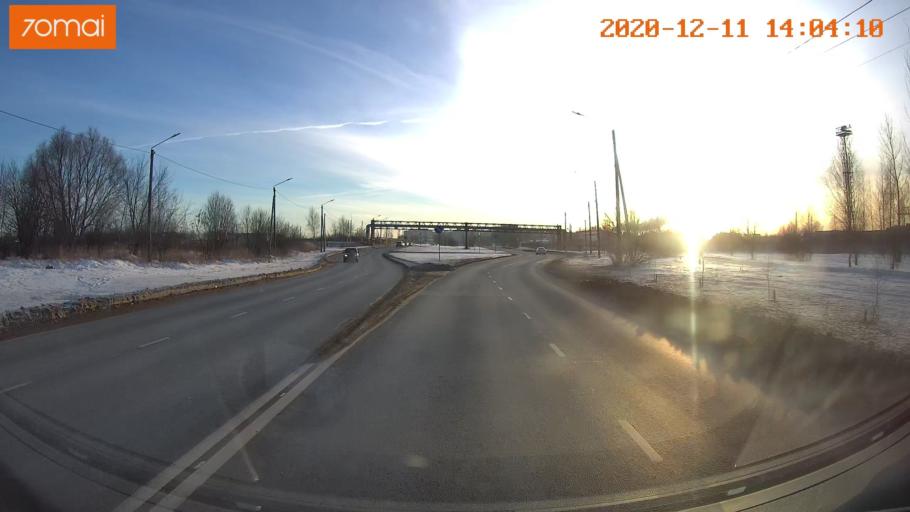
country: RU
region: Kostroma
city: Oktyabr'skiy
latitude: 57.7581
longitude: 41.0164
